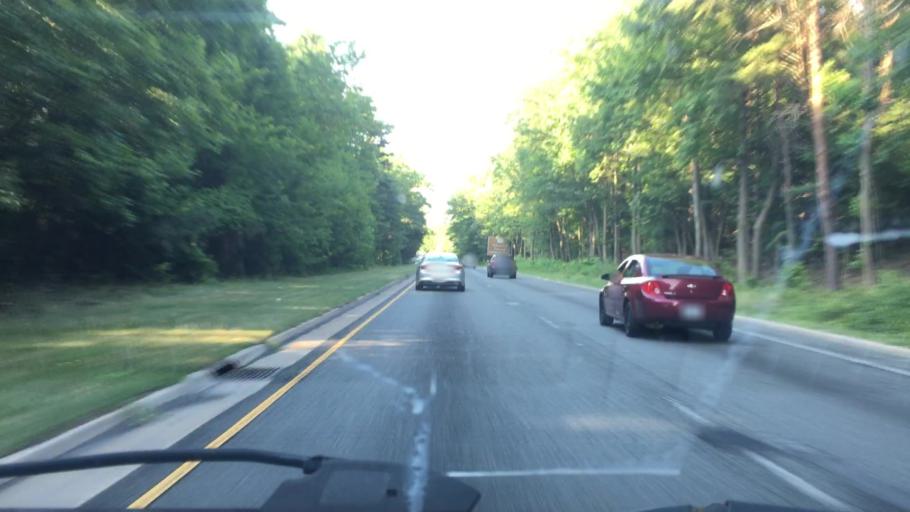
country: US
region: Maryland
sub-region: Anne Arundel County
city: Jessup
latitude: 39.1275
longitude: -76.7627
